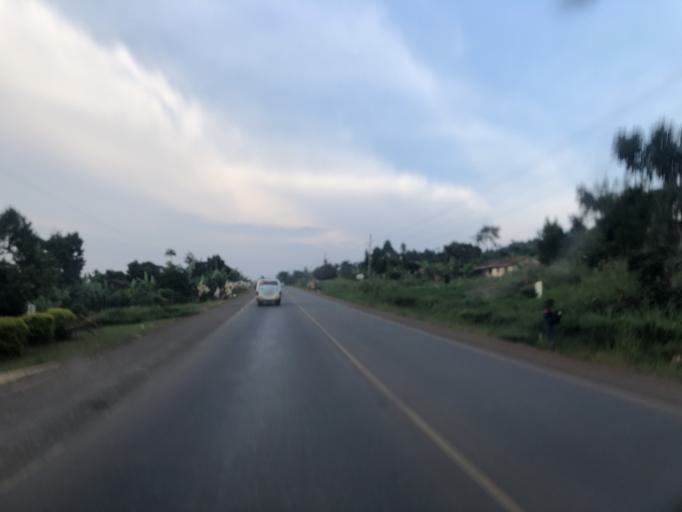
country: UG
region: Central Region
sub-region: Mpigi District
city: Mpigi
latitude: 0.2292
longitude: 32.3446
